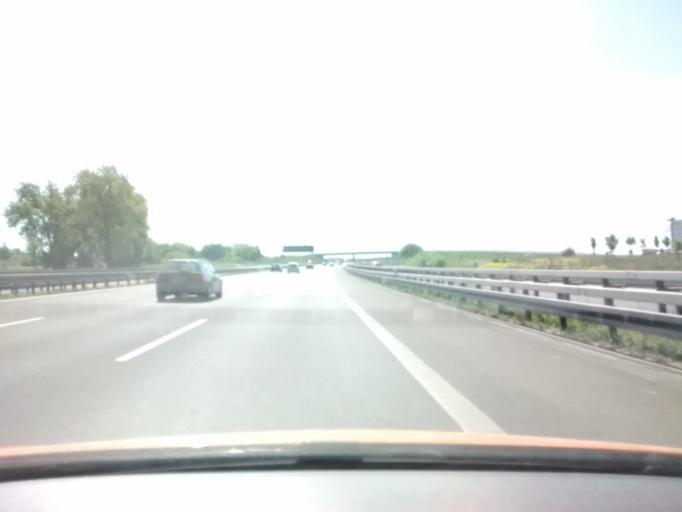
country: DE
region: Brandenburg
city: Schonefeld
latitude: 52.3734
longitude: 13.5465
